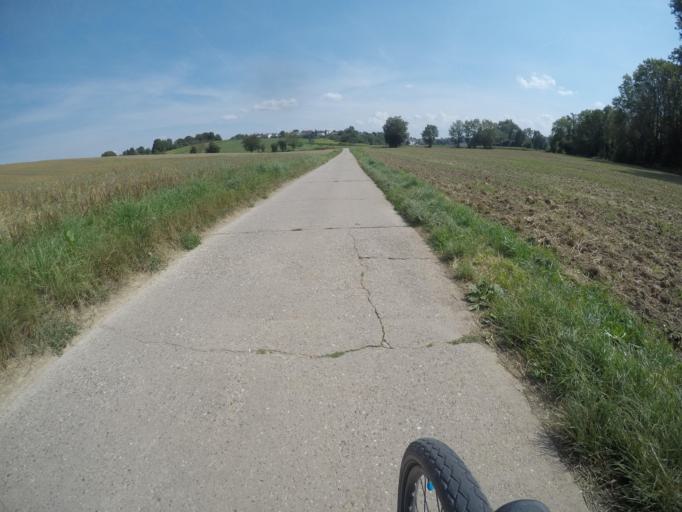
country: DE
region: Baden-Wuerttemberg
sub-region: Karlsruhe Region
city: Gondelsheim
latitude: 49.0502
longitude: 8.6704
